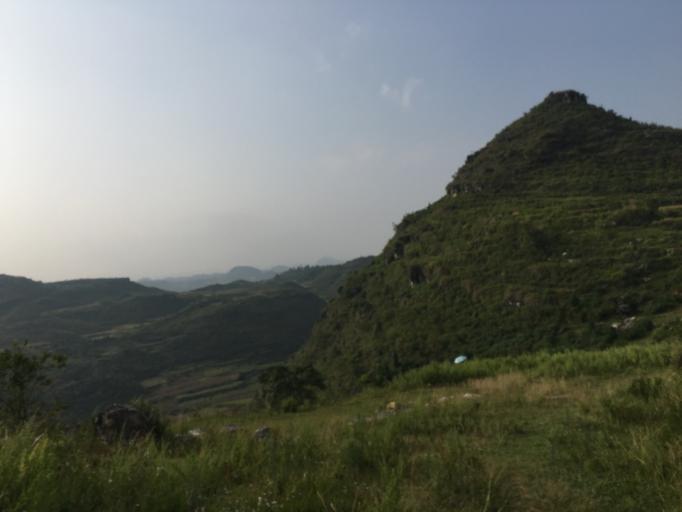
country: CN
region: Guangxi Zhuangzu Zizhiqu
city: Xinzhou
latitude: 25.4389
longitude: 105.6381
